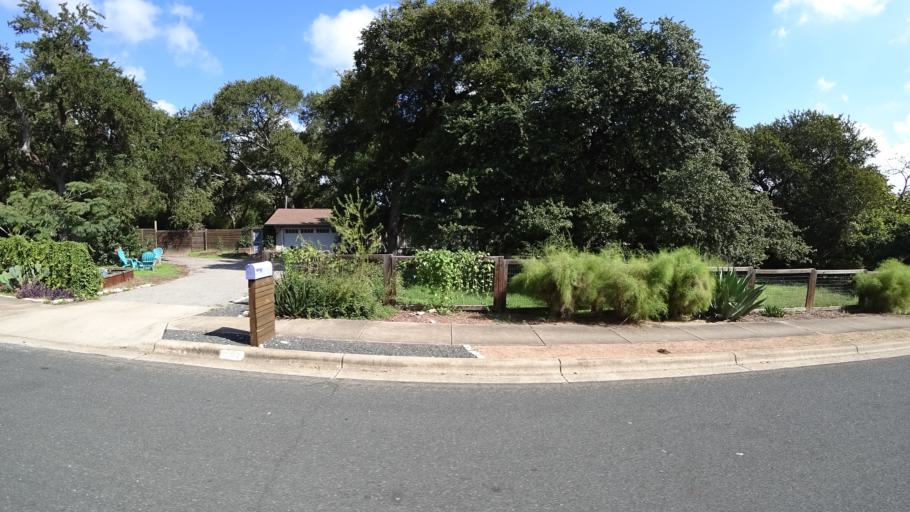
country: US
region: Texas
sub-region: Travis County
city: Shady Hollow
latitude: 30.2017
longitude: -97.8089
